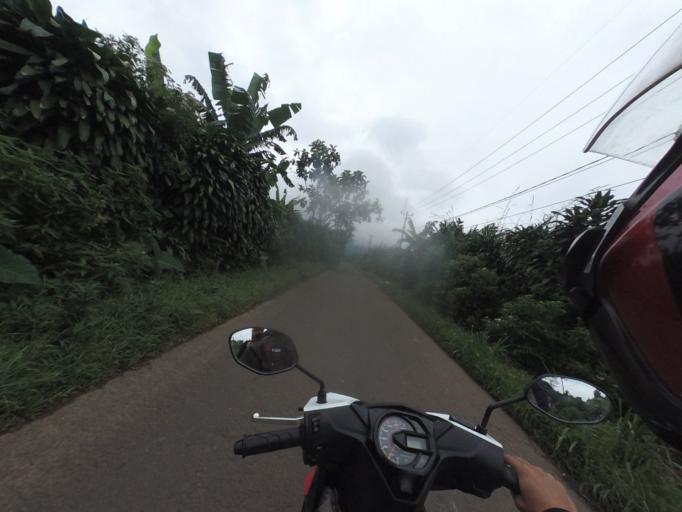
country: ID
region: West Java
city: Bogor
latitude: -6.6508
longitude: 106.7277
